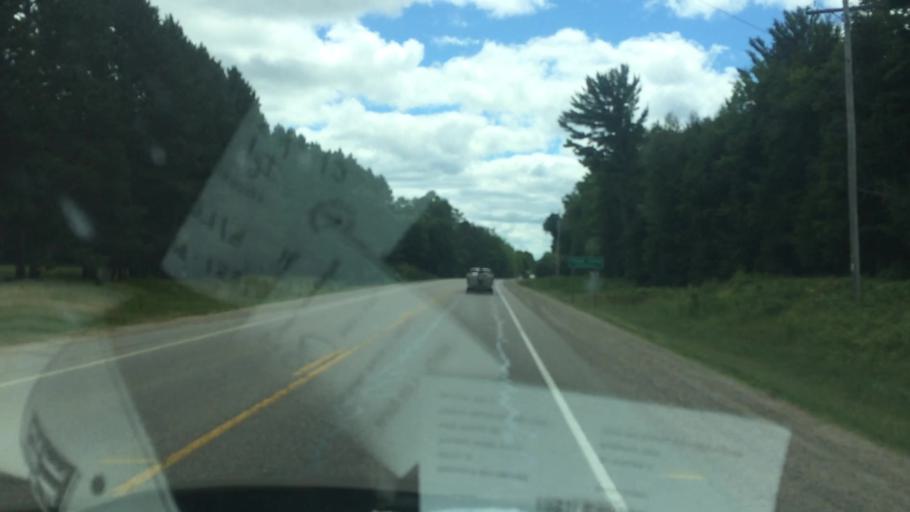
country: US
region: Wisconsin
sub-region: Vilas County
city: Eagle River
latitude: 45.8066
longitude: -89.3199
